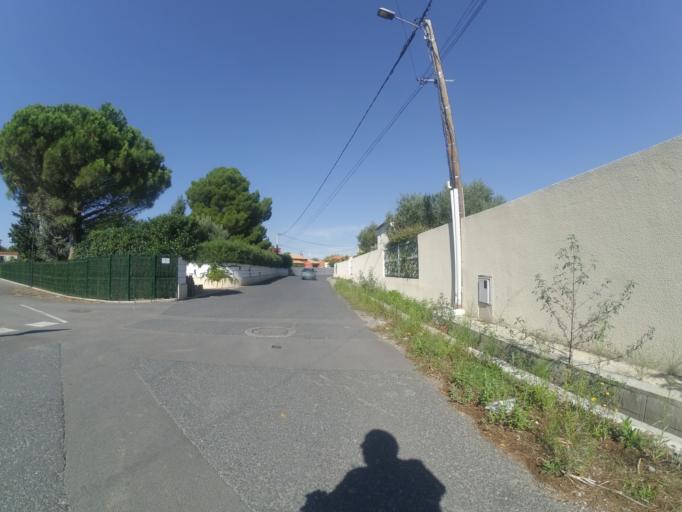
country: FR
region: Languedoc-Roussillon
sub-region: Departement des Pyrenees-Orientales
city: Pezilla-la-Riviere
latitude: 42.6935
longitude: 2.7674
